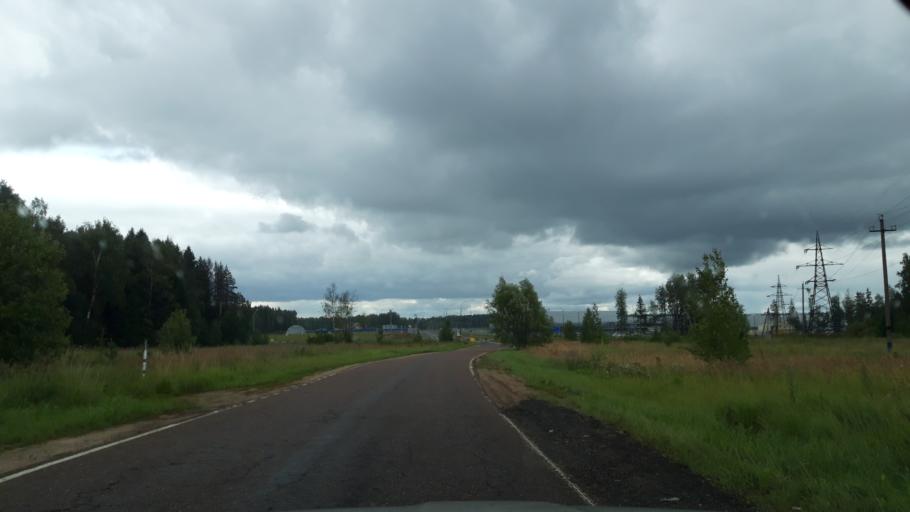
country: RU
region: Moskovskaya
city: Lozhki
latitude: 56.0899
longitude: 37.0771
